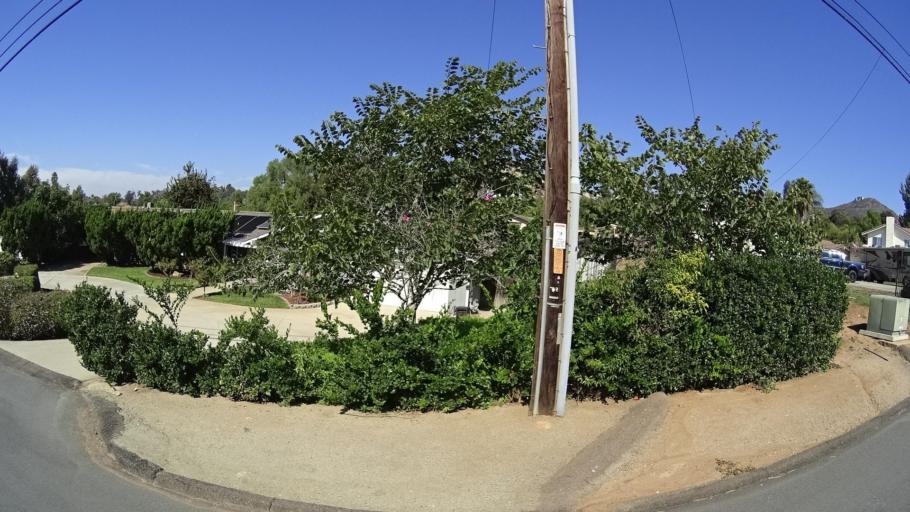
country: US
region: California
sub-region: San Diego County
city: Rancho San Diego
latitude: 32.7622
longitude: -116.9137
